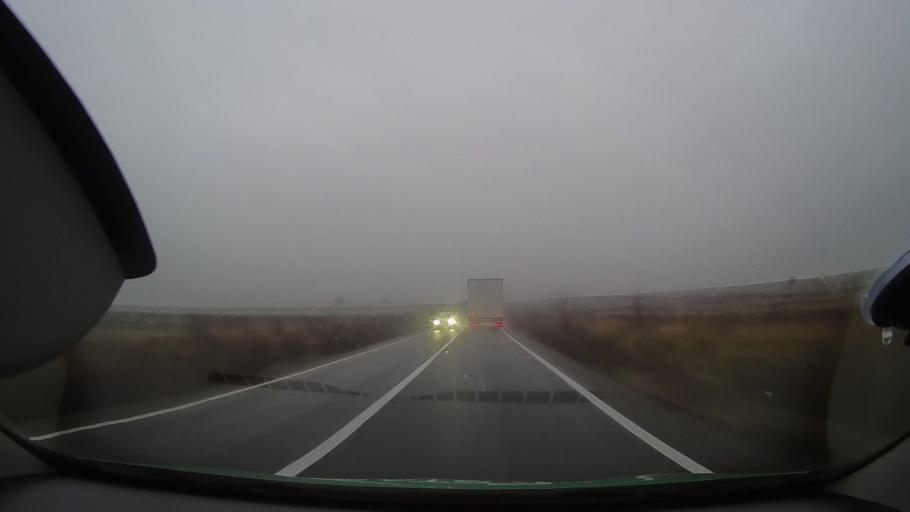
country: RO
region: Bihor
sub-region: Comuna Olcea
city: Olcea
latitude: 46.6692
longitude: 21.9640
